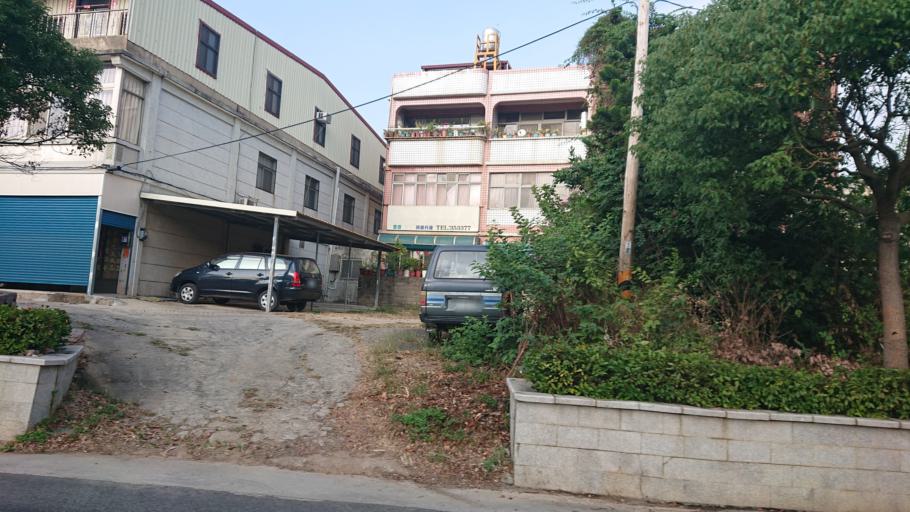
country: TW
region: Fukien
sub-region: Kinmen
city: Jincheng
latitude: 24.4778
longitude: 118.4274
